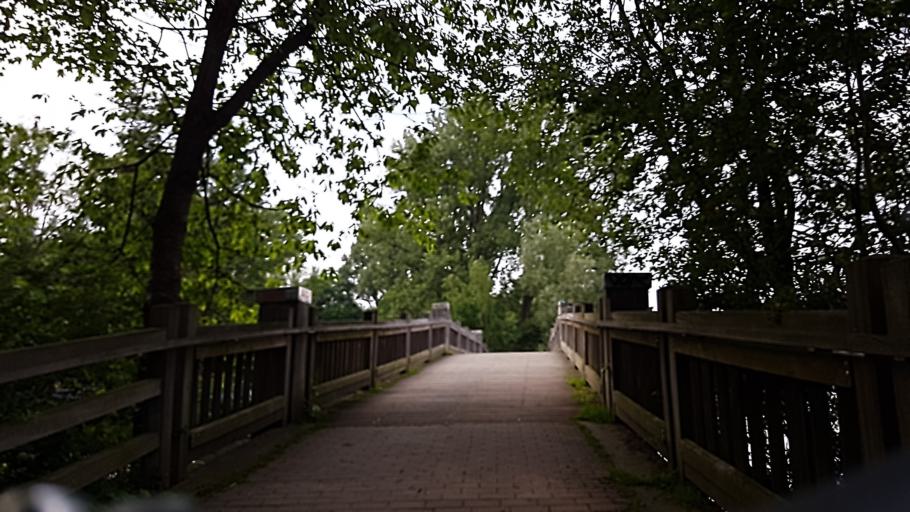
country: DE
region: Hamburg
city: Hamburg-Nord
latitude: 53.5941
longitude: 9.9915
